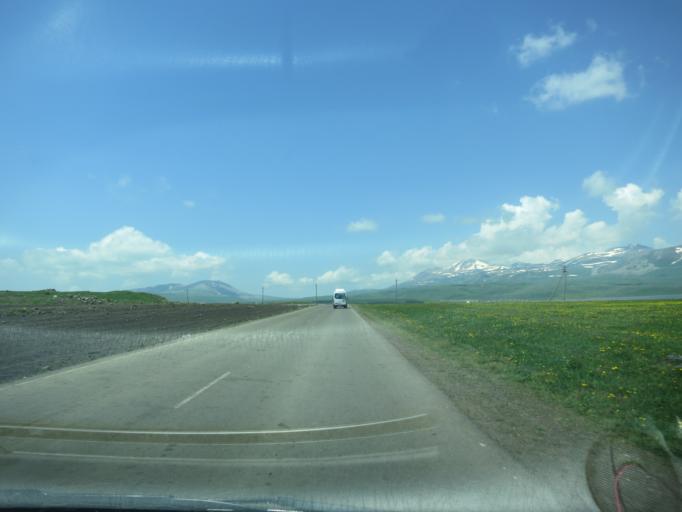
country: GE
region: Samtskhe-Javakheti
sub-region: Ninotsminda
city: Ninotsminda
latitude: 41.4052
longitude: 43.8116
